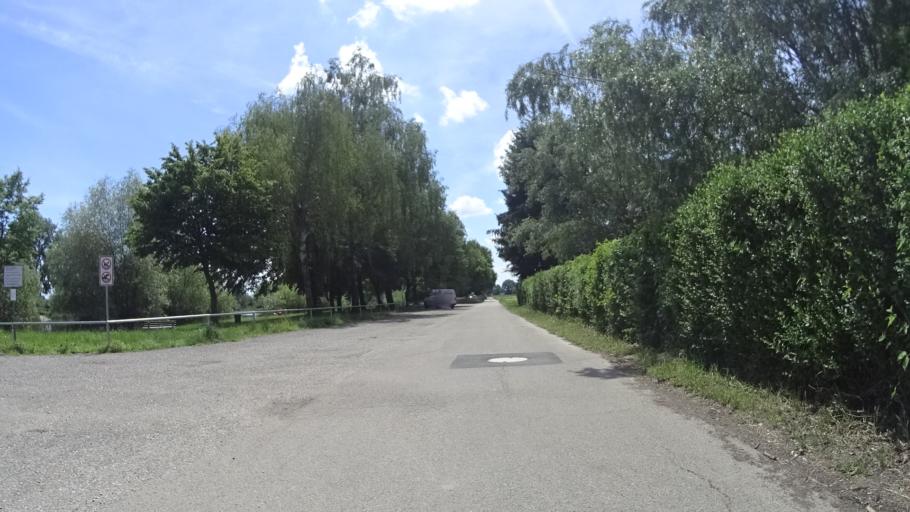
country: DE
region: Baden-Wuerttemberg
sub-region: Freiburg Region
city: Rust
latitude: 48.2859
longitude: 7.7401
